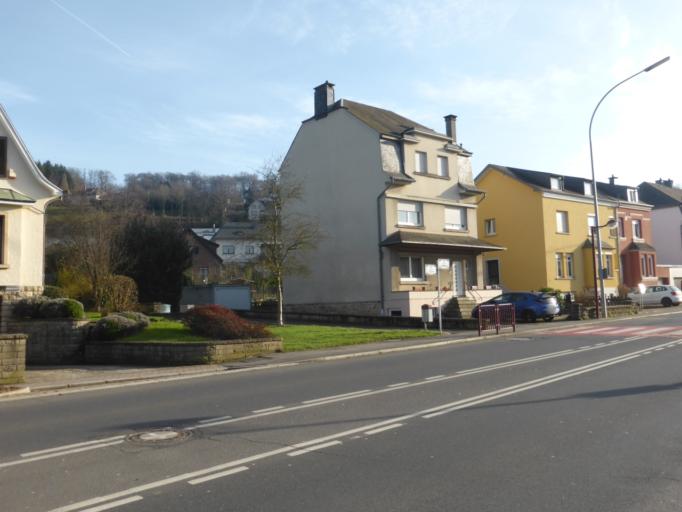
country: LU
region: Luxembourg
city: Colmar
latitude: 49.8138
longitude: 6.0987
